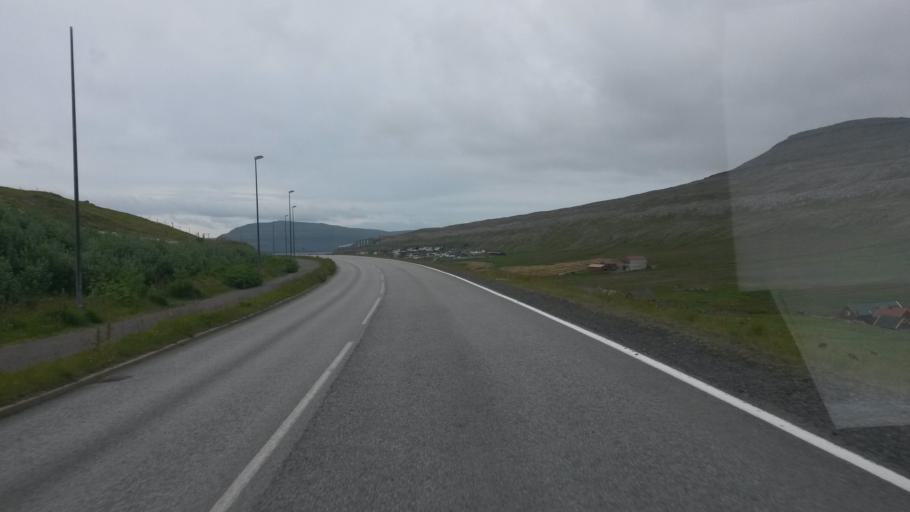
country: FO
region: Streymoy
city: Argir
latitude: 61.9990
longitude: -6.8234
